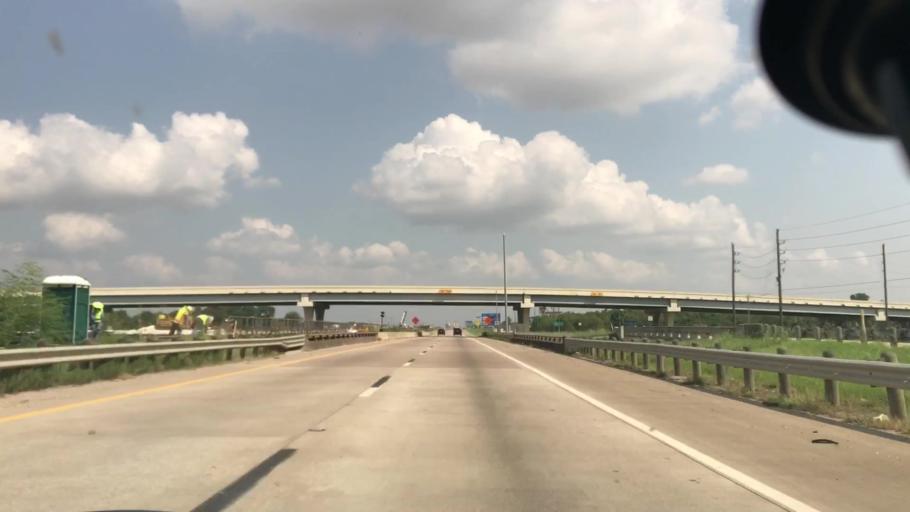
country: US
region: Texas
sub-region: Brazoria County
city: Iowa Colony
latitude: 29.5244
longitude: -95.3866
